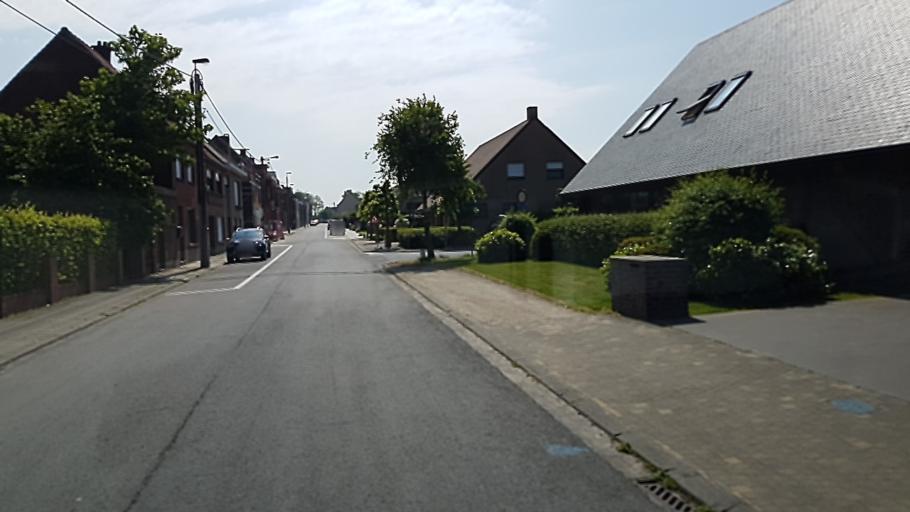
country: BE
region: Flanders
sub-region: Provincie West-Vlaanderen
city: Deerlijk
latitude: 50.8416
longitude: 3.3993
